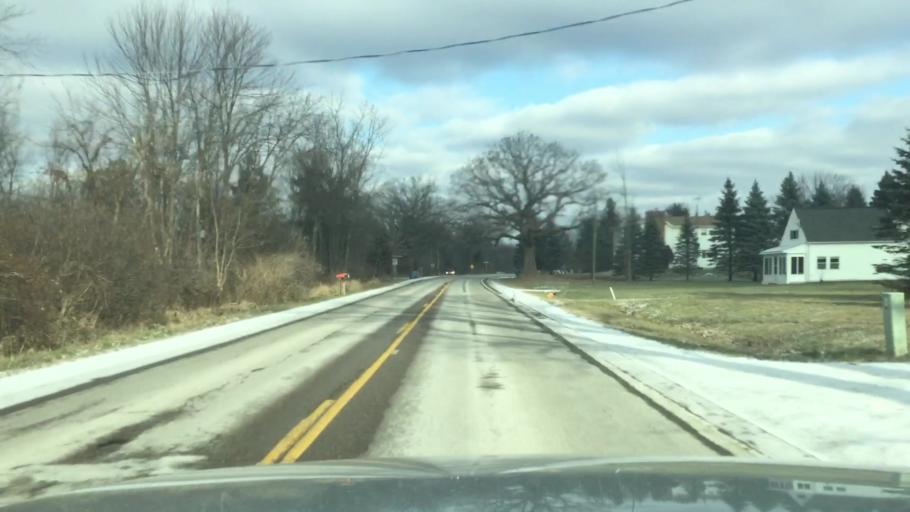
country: US
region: Michigan
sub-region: Genesee County
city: Linden
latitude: 42.8481
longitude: -83.7833
